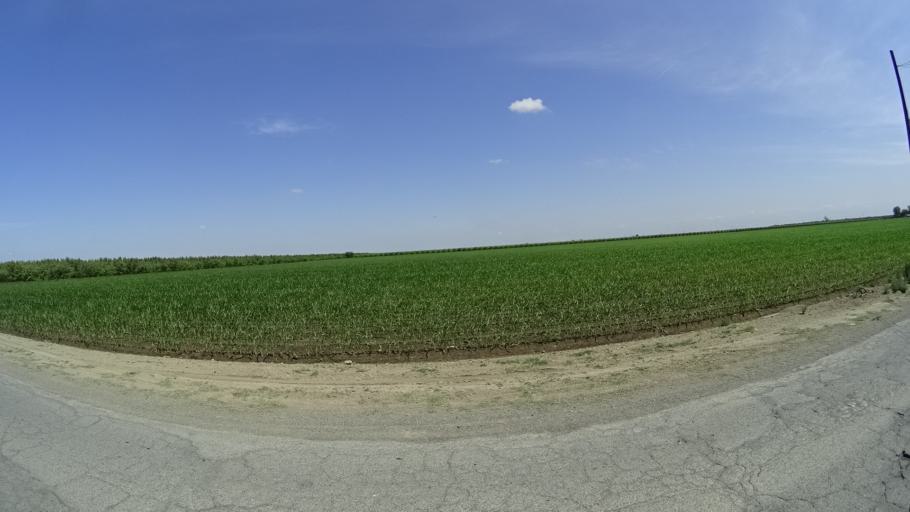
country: US
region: California
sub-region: Tulare County
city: Goshen
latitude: 36.2691
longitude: -119.5008
